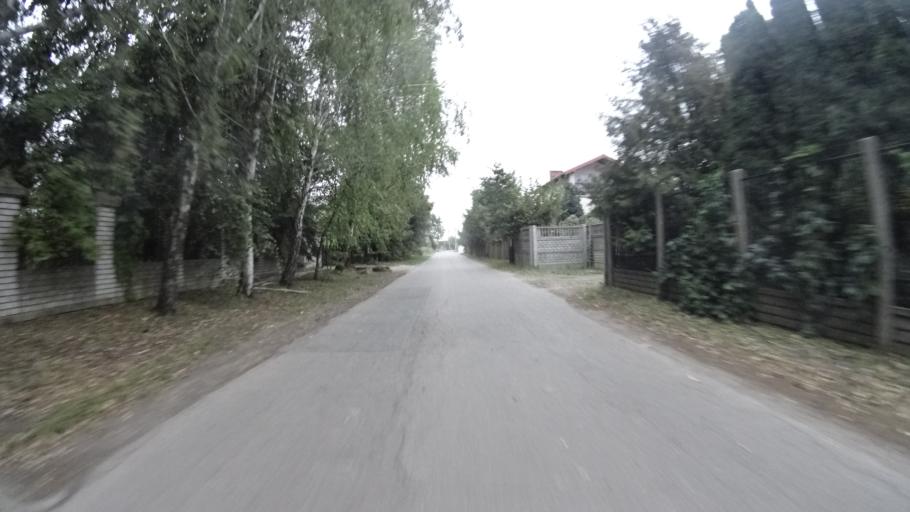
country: PL
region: Masovian Voivodeship
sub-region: Powiat warszawski zachodni
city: Stare Babice
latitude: 52.2629
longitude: 20.8225
